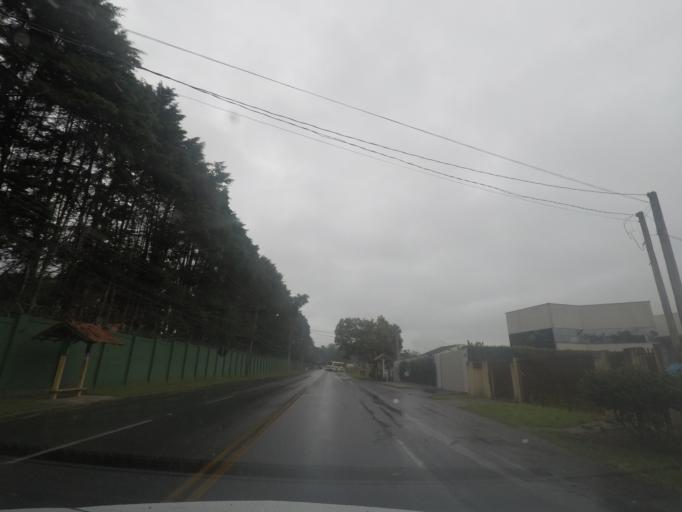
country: BR
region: Parana
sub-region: Quatro Barras
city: Quatro Barras
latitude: -25.3743
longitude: -49.0996
